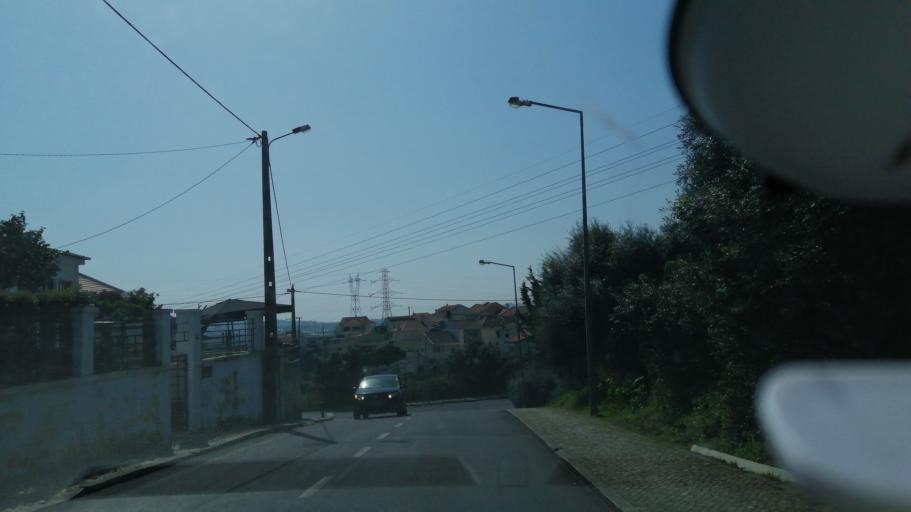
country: PT
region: Lisbon
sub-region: Odivelas
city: Famoes
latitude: 38.7917
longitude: -9.2034
